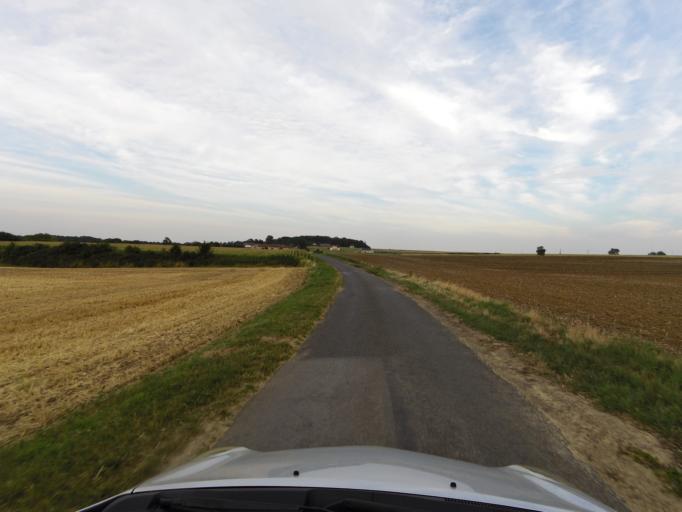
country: FR
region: Picardie
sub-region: Departement de l'Aisne
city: Bruyeres-et-Montberault
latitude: 49.4996
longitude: 3.6589
